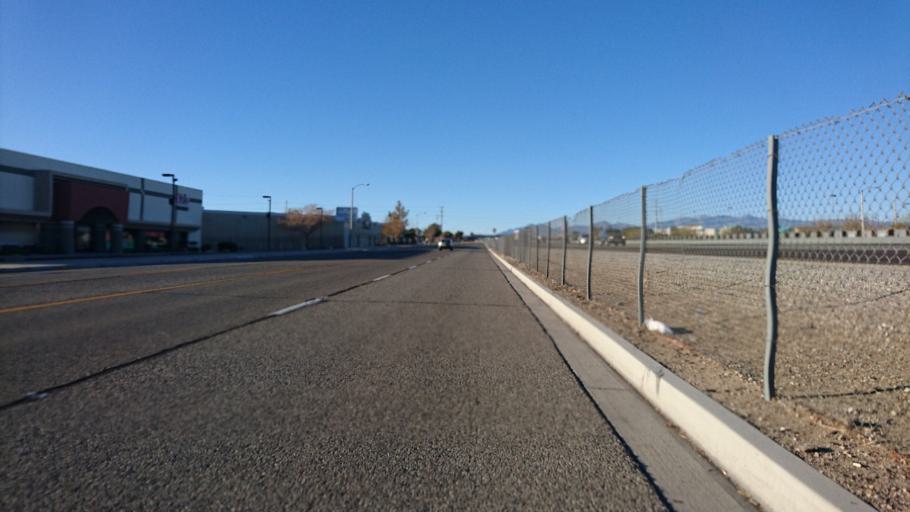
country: US
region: California
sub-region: San Bernardino County
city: Mountain View Acres
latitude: 34.4776
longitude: -117.3403
